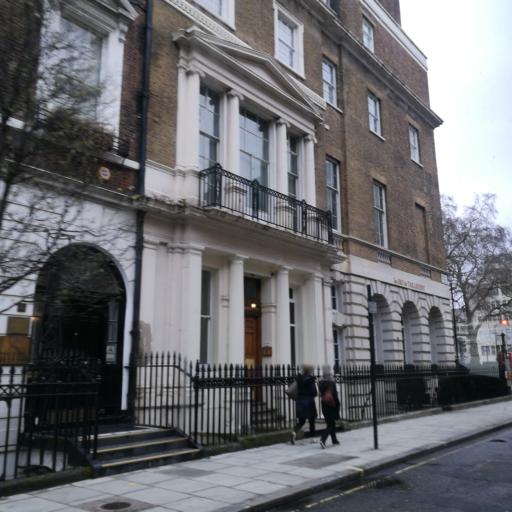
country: GB
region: England
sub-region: Greater London
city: London
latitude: 51.5172
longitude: -0.1462
